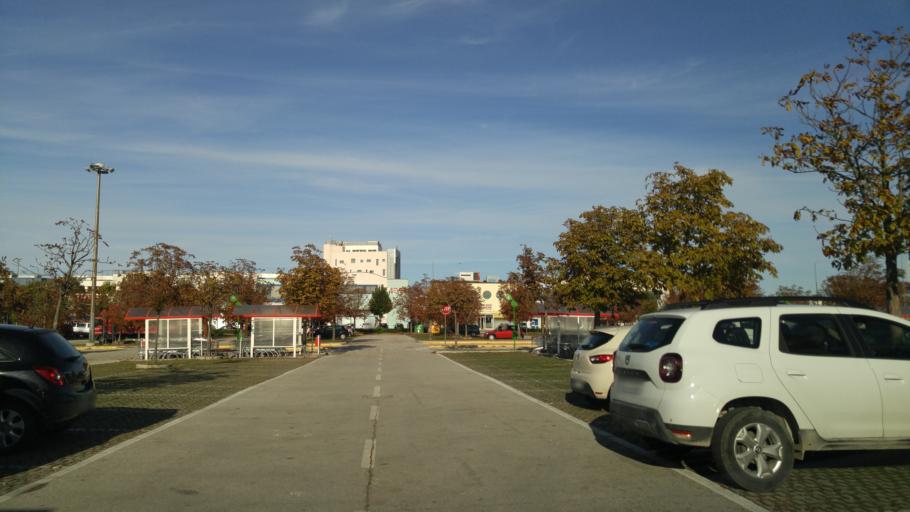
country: IT
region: The Marches
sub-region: Provincia di Pesaro e Urbino
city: Bellocchi
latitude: 43.8010
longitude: 13.0129
